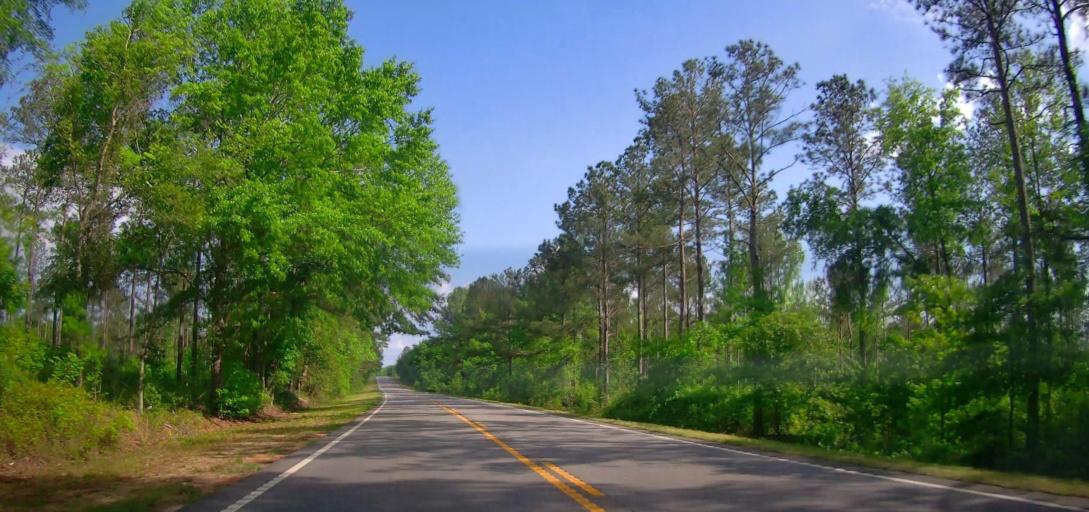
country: US
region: Georgia
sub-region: Baldwin County
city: Hardwick
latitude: 33.0469
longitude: -83.1208
